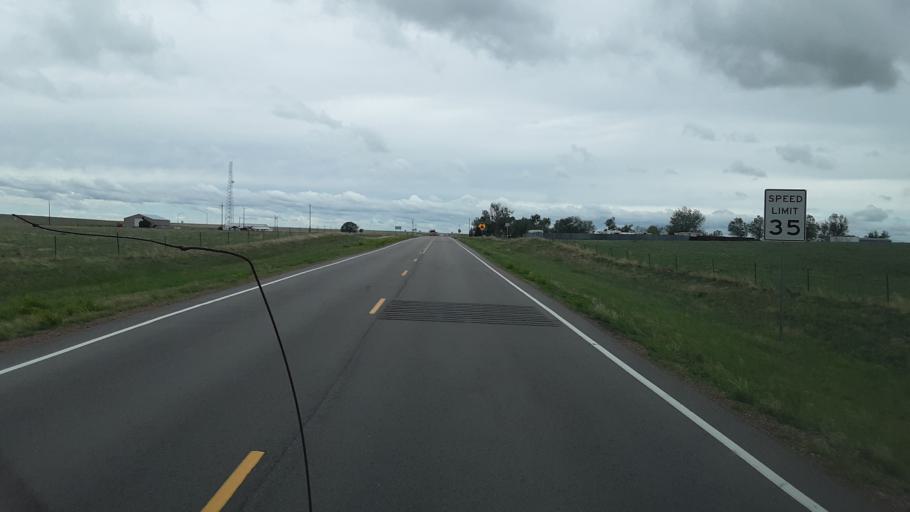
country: US
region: Colorado
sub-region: Lincoln County
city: Hugo
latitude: 38.8519
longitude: -103.6965
